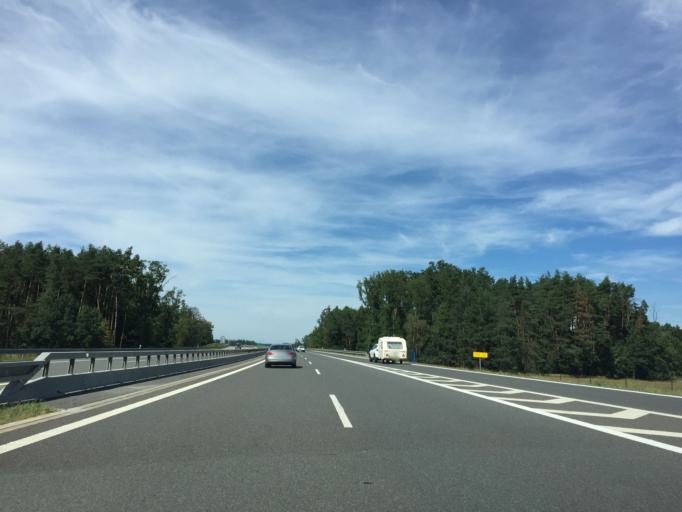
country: CZ
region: Jihocesky
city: Sobeslav
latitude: 49.2251
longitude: 14.7281
